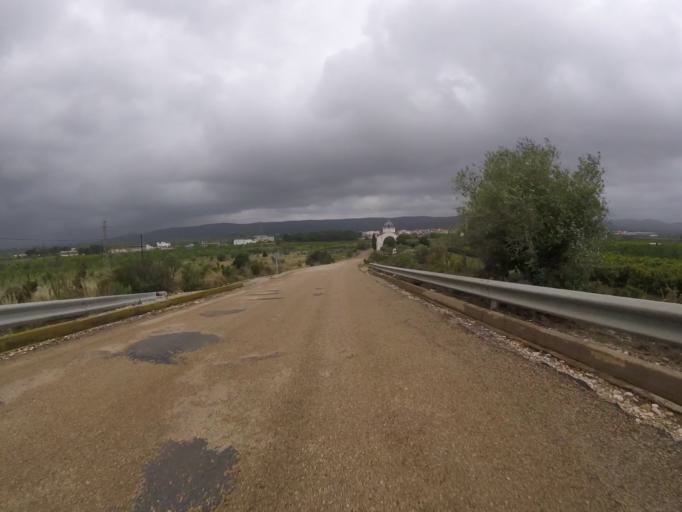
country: ES
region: Valencia
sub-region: Provincia de Castello
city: Alcala de Xivert
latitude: 40.2965
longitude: 0.2328
